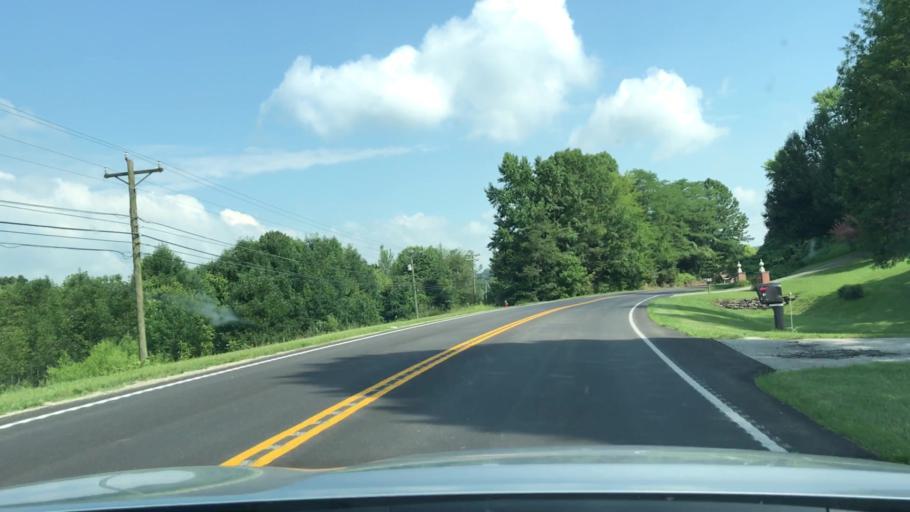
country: US
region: Kentucky
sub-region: Barren County
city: Glasgow
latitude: 37.0282
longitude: -85.9078
